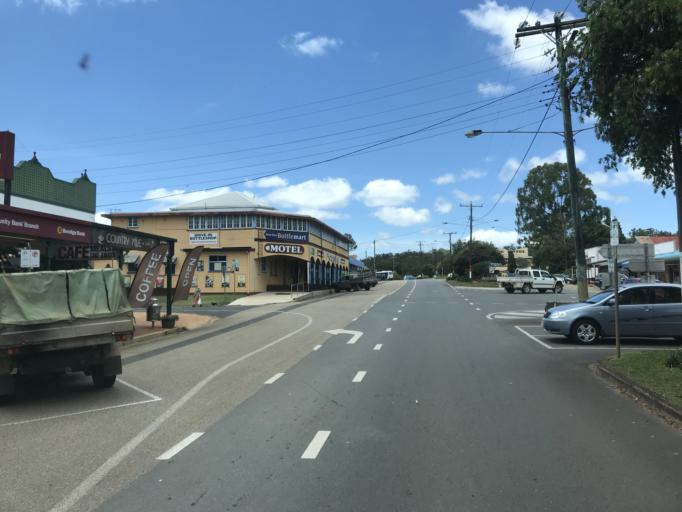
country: AU
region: Queensland
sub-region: Tablelands
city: Ravenshoe
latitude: -17.6067
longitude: 145.4826
